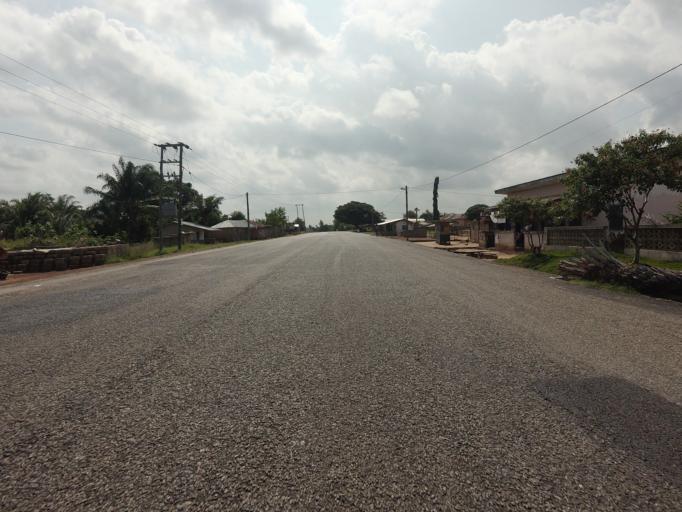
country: GH
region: Volta
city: Ho
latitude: 6.4144
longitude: 0.7565
